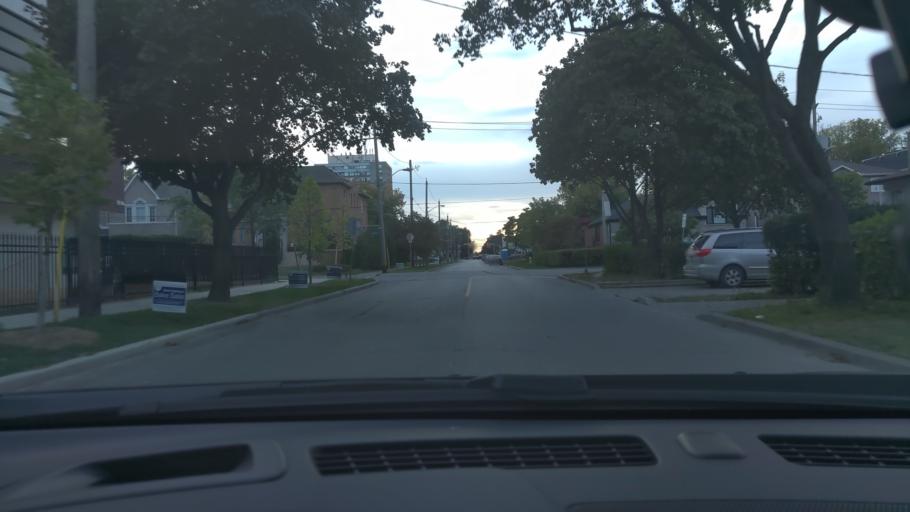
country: CA
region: Ontario
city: Toronto
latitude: 43.7184
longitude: -79.4261
